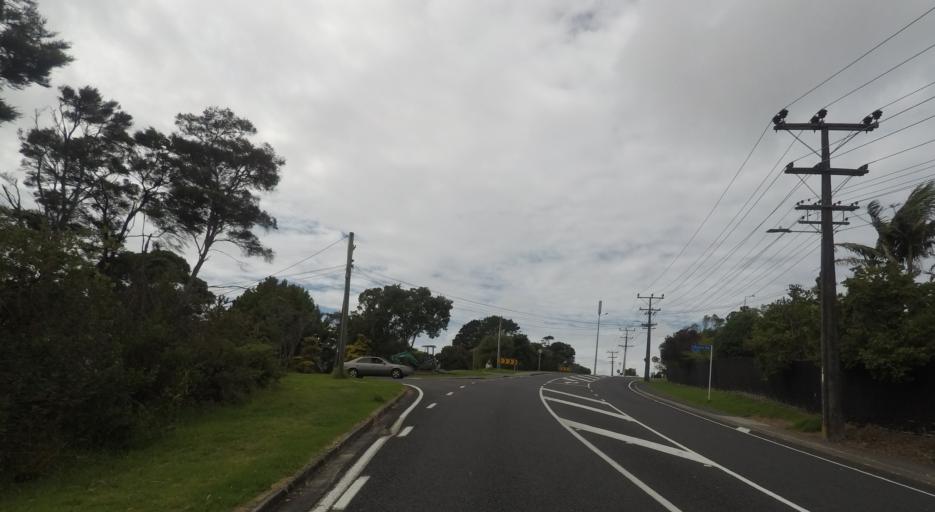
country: NZ
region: Auckland
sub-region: Auckland
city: North Shore
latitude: -36.7703
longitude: 174.6941
